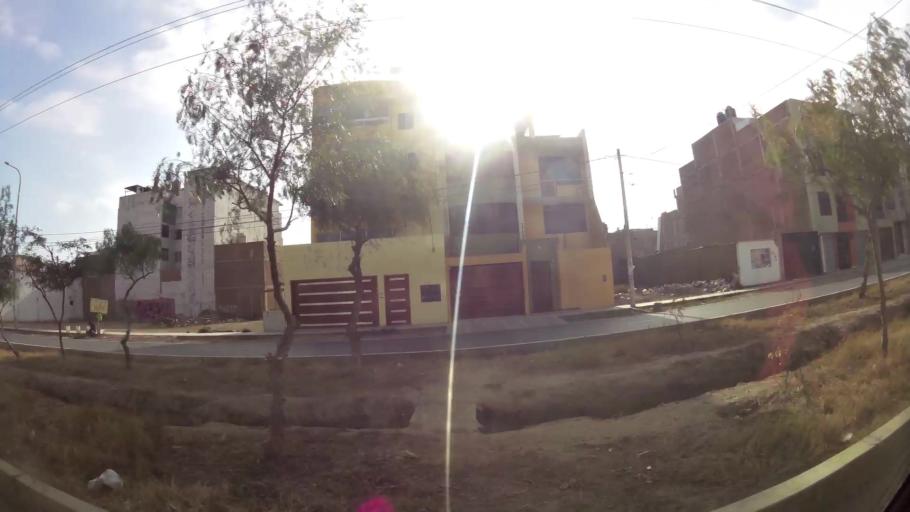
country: PE
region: La Libertad
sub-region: Provincia de Trujillo
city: La Esperanza
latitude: -8.0933
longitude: -79.0479
